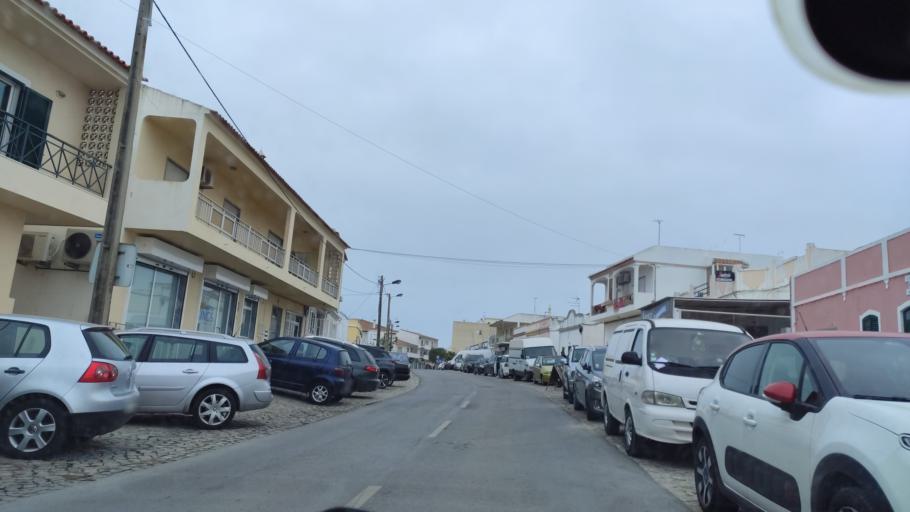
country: PT
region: Faro
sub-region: Faro
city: Faro
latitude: 37.0316
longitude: -7.9604
